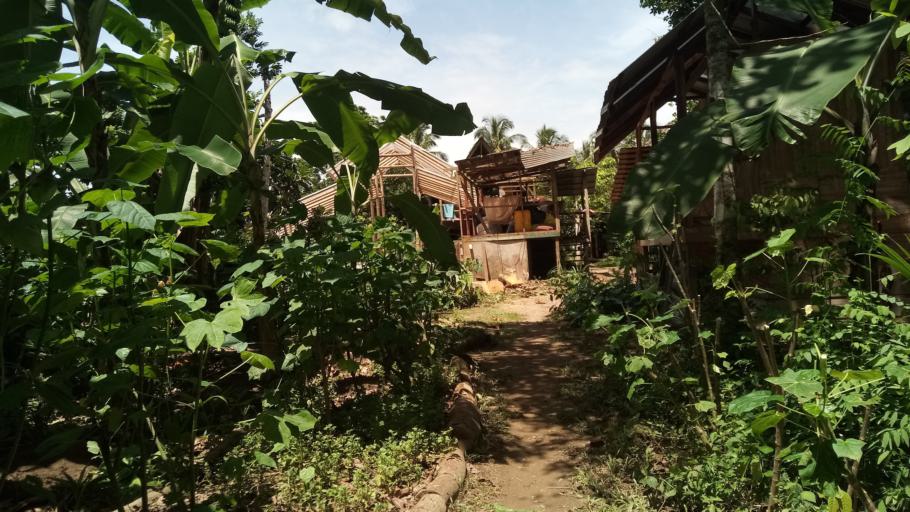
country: CR
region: Limon
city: Sixaola
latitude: 9.6241
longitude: -82.6204
